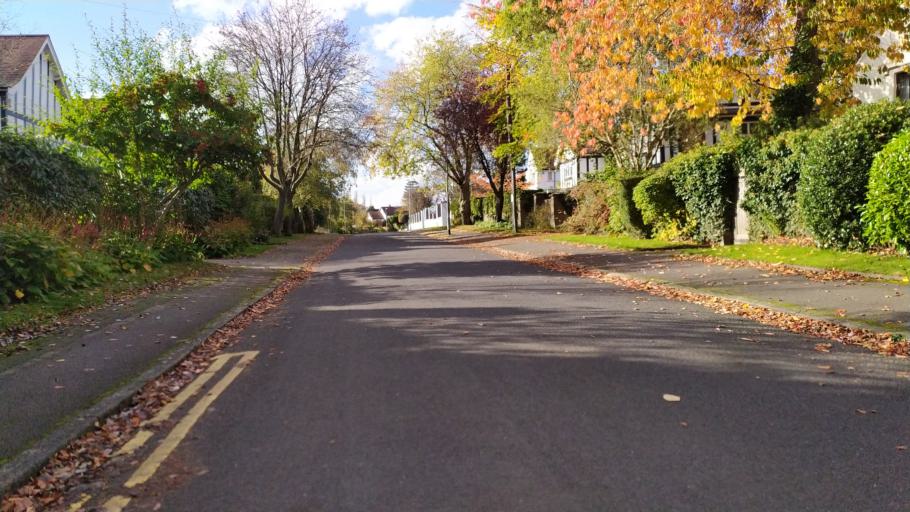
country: GB
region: England
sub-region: City and Borough of Leeds
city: Horsforth
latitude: 53.8302
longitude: -1.5929
